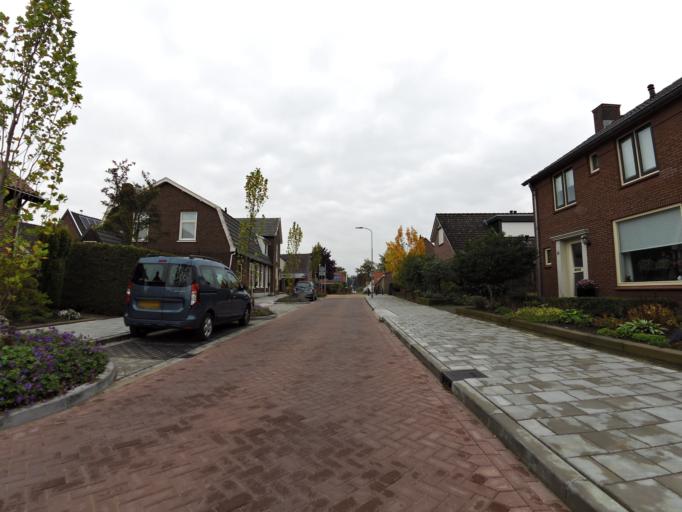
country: NL
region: Gelderland
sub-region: Oude IJsselstreek
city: Gendringen
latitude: 51.8883
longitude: 6.3832
